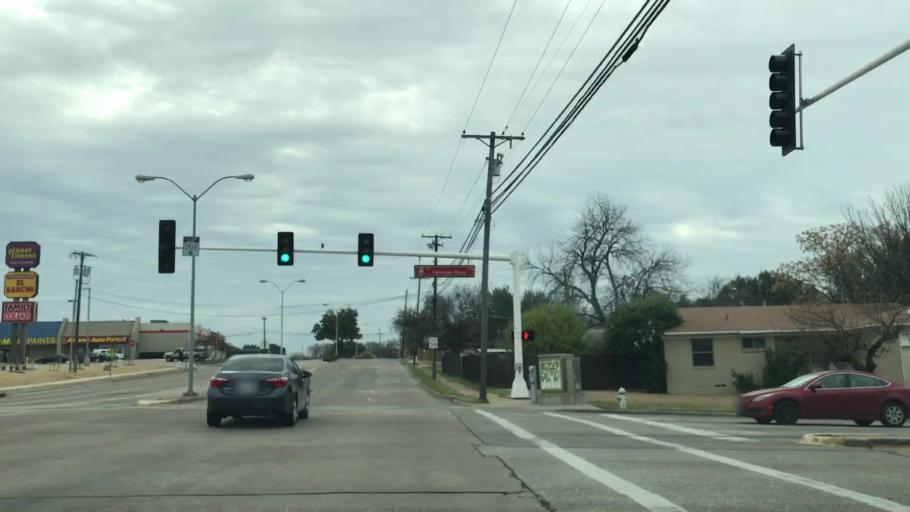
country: US
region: Texas
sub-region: Dallas County
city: Farmers Branch
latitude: 32.9383
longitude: -96.8906
